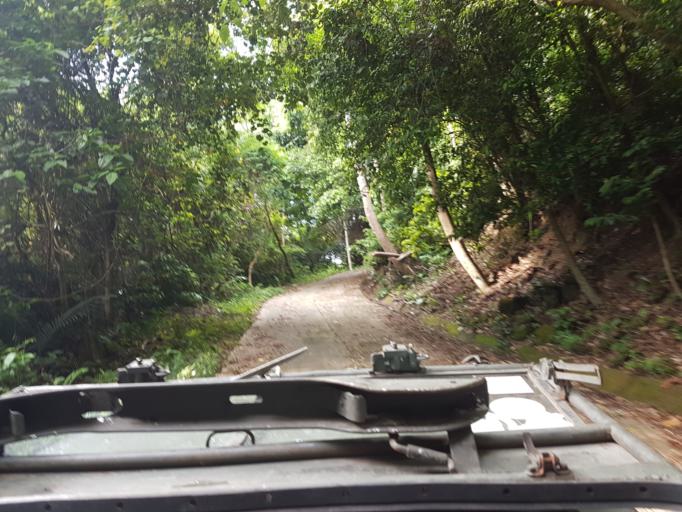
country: TH
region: Pattani
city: Khok Pho
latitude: 6.6572
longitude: 101.0974
